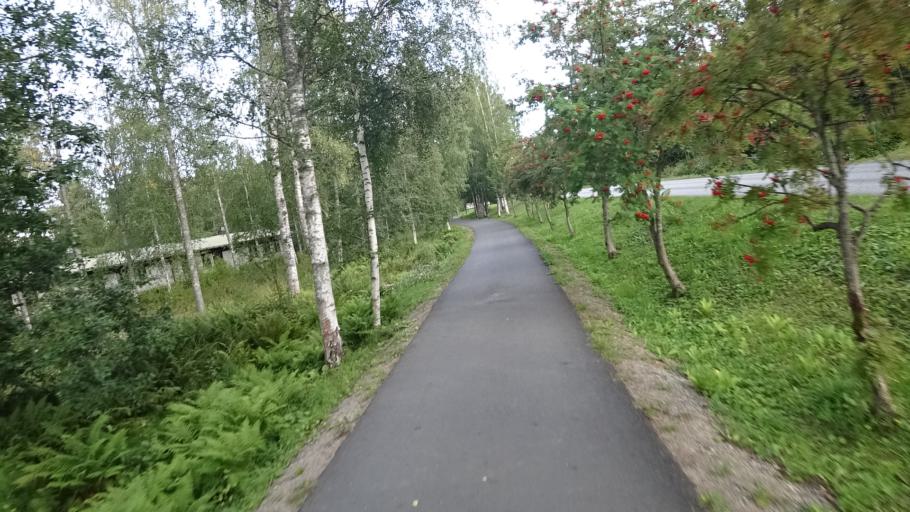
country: FI
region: North Karelia
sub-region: Joensuu
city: Ilomantsi
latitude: 62.6745
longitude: 30.9216
